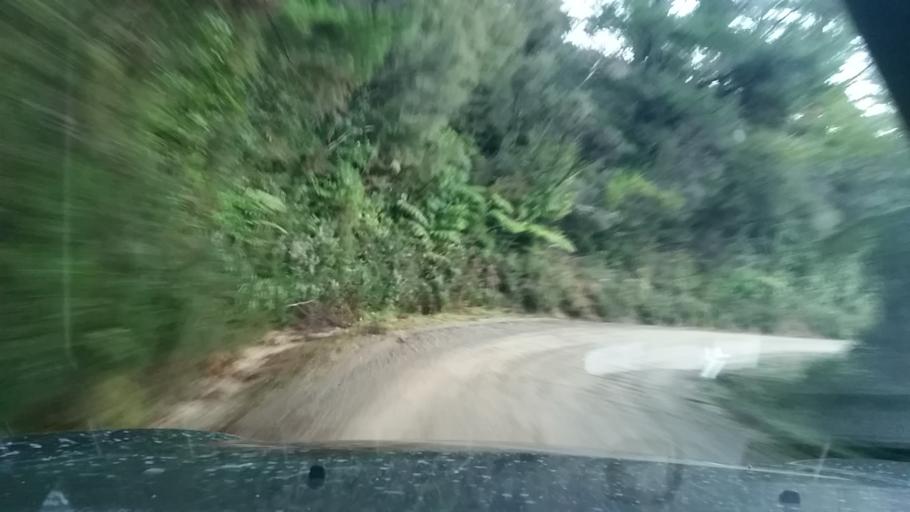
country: NZ
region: Marlborough
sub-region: Marlborough District
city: Picton
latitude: -41.1371
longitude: 174.1425
